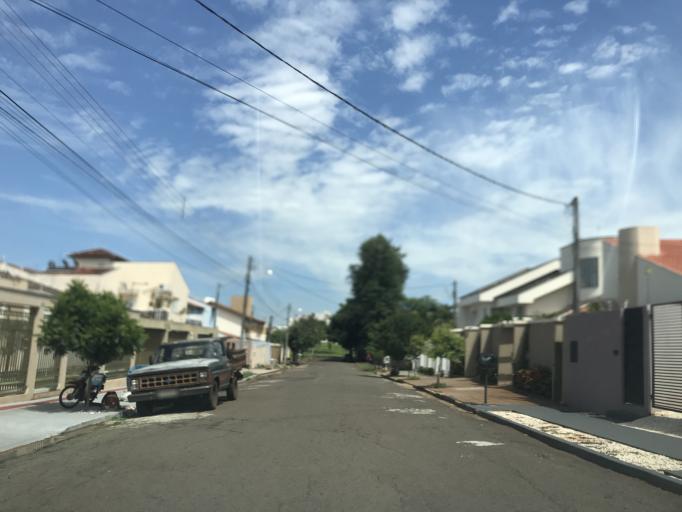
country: BR
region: Parana
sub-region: Londrina
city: Londrina
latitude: -23.3474
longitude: -51.1623
